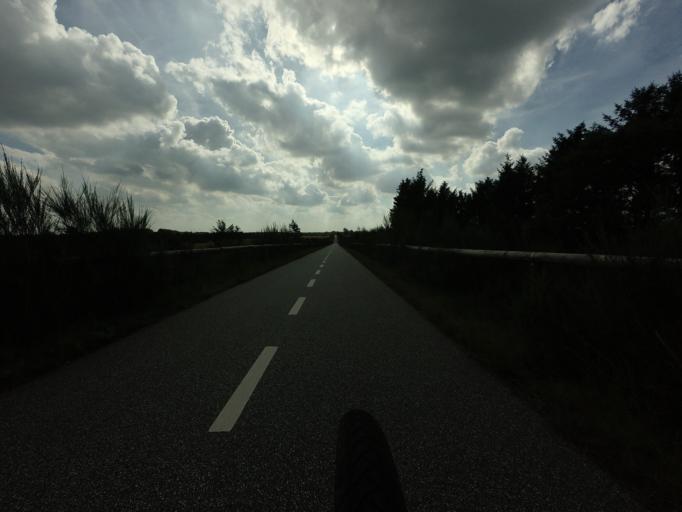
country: DK
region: Central Jutland
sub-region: Herning Kommune
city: Sunds
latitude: 56.1892
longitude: 9.0108
